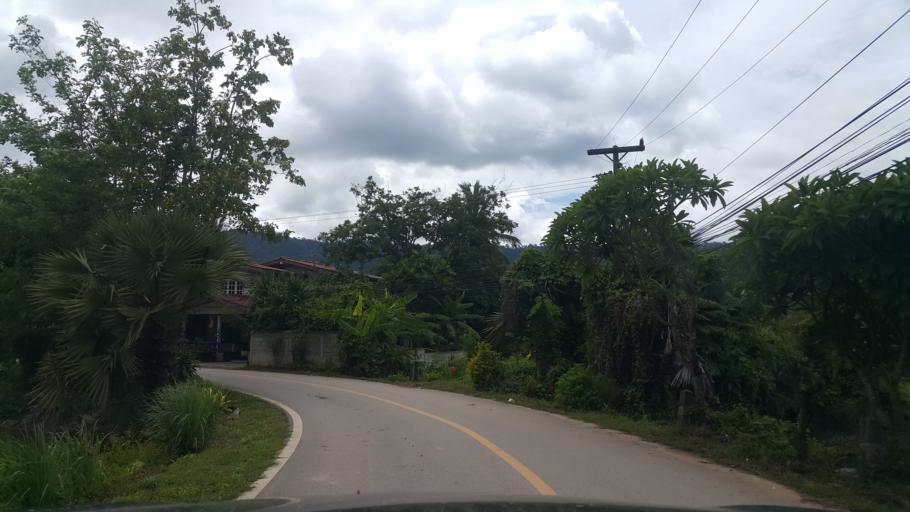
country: TH
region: Phitsanulok
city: Chat Trakan
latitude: 17.3040
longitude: 100.6685
